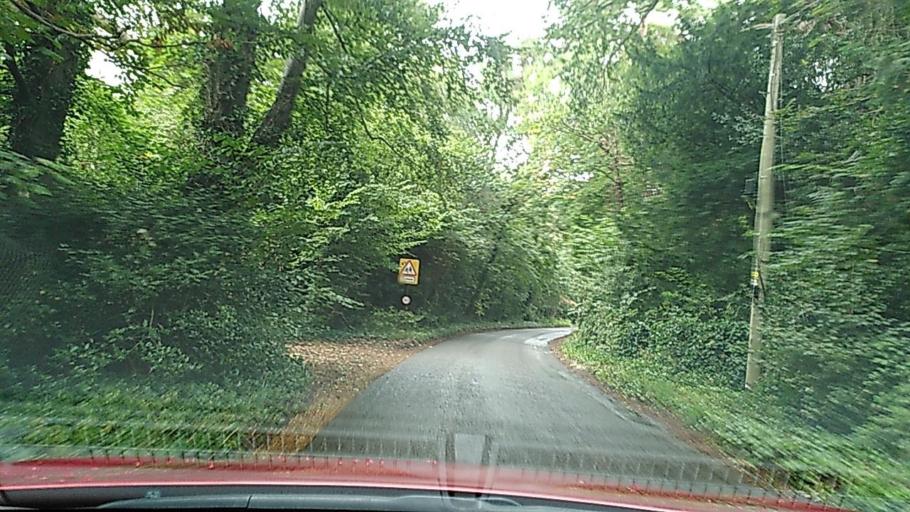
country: GB
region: England
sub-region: Oxfordshire
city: Henley on Thames
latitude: 51.5240
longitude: -0.9217
